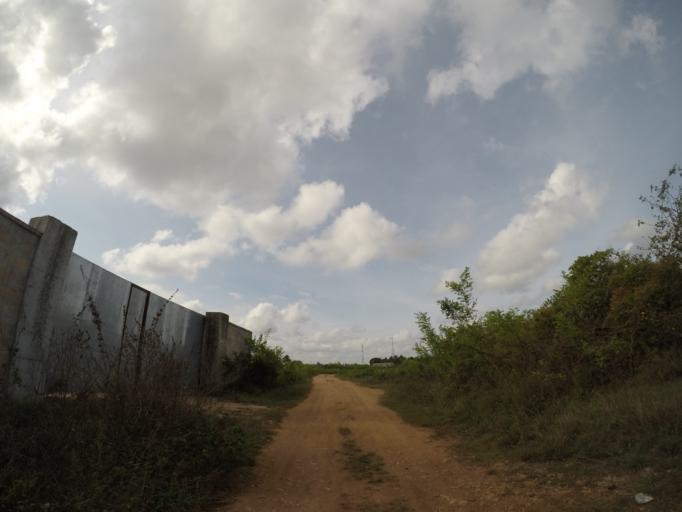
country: TZ
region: Zanzibar Central/South
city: Koani
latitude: -6.2332
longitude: 39.3188
